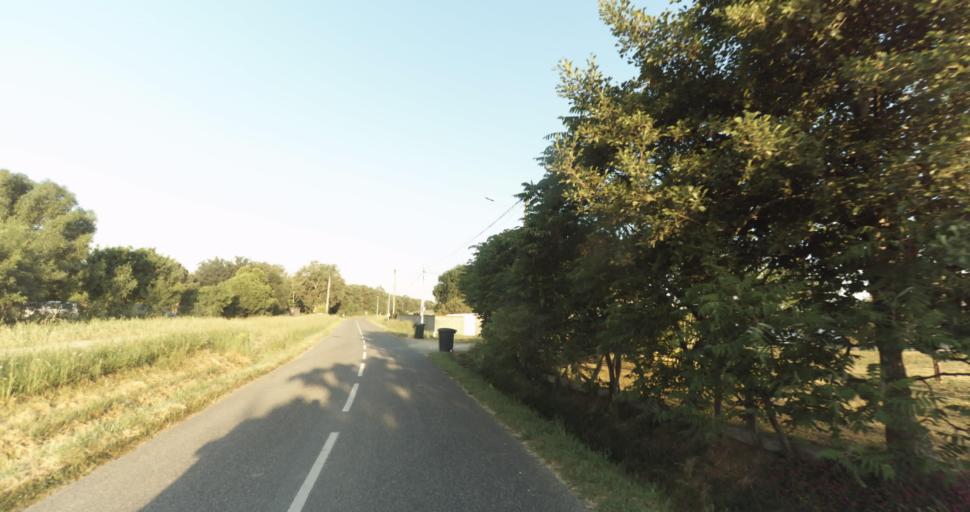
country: FR
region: Midi-Pyrenees
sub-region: Departement de la Haute-Garonne
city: Leguevin
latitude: 43.5807
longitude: 1.2093
